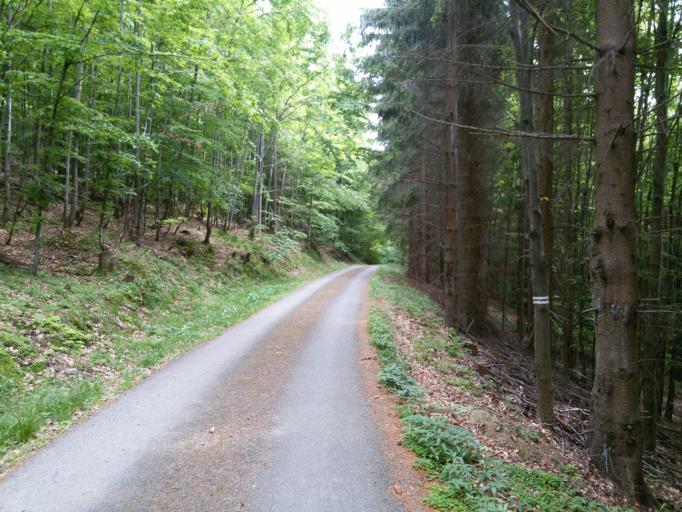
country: CZ
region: Olomoucky
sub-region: Okres Sumperk
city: Loucna nad Desnou
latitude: 50.1124
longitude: 17.1132
